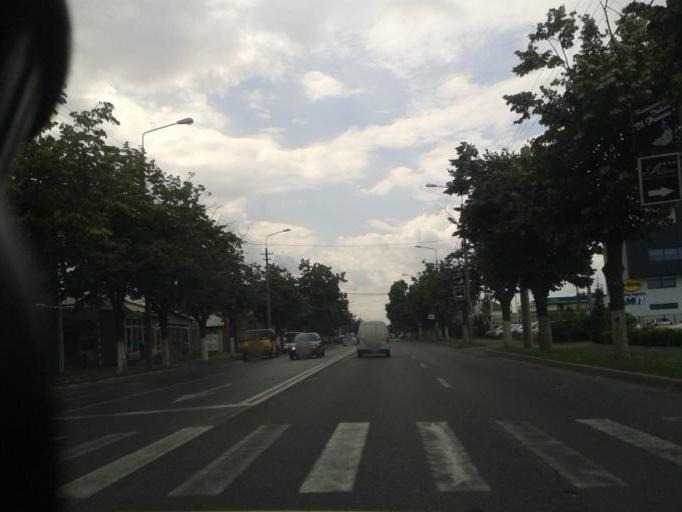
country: RO
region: Prahova
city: Ploiesti
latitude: 44.9572
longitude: 25.9878
